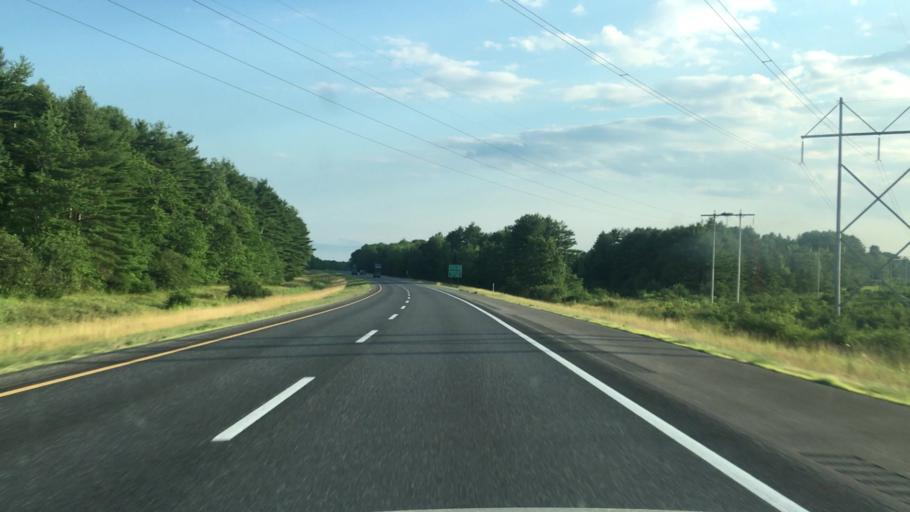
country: US
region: Maine
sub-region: Sagadahoc County
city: Topsham
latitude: 43.9675
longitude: -69.9556
